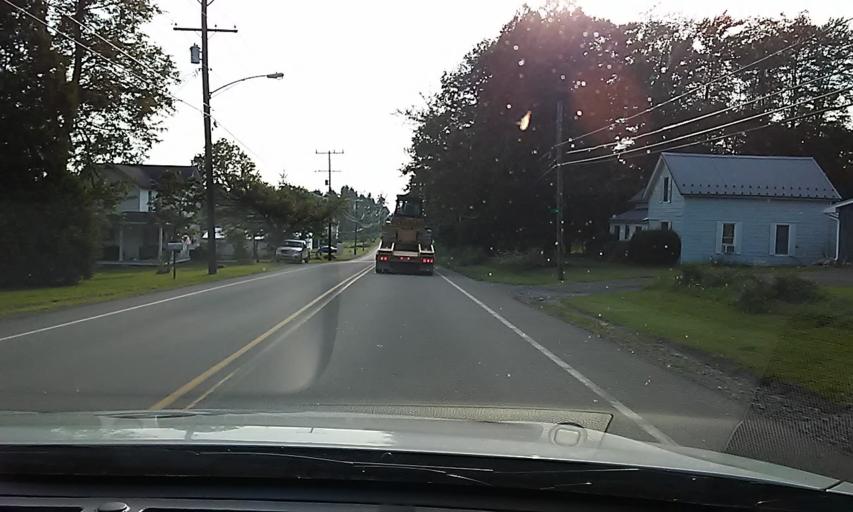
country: US
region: Pennsylvania
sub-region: McKean County
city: Kane
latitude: 41.7244
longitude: -78.6588
